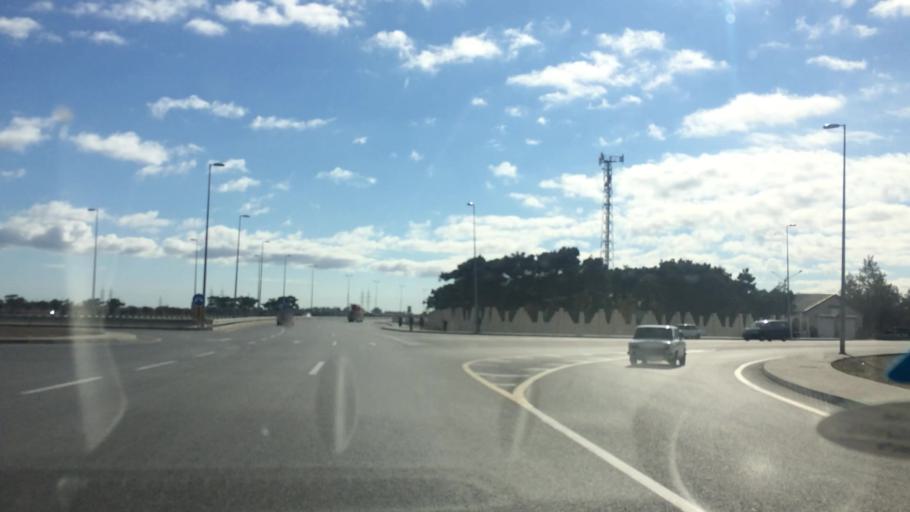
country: AZ
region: Baki
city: Qala
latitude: 40.4443
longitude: 50.1763
